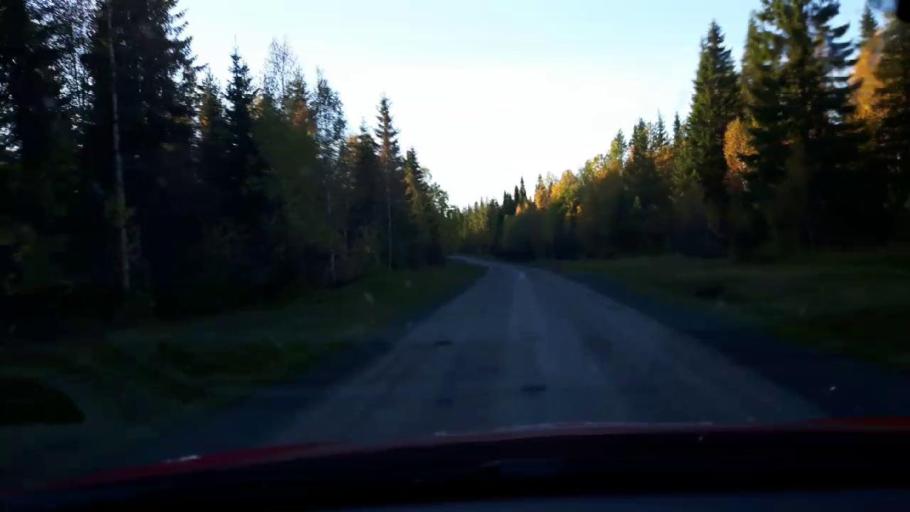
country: SE
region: Jaemtland
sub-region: Krokoms Kommun
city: Krokom
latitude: 63.4484
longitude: 14.5746
